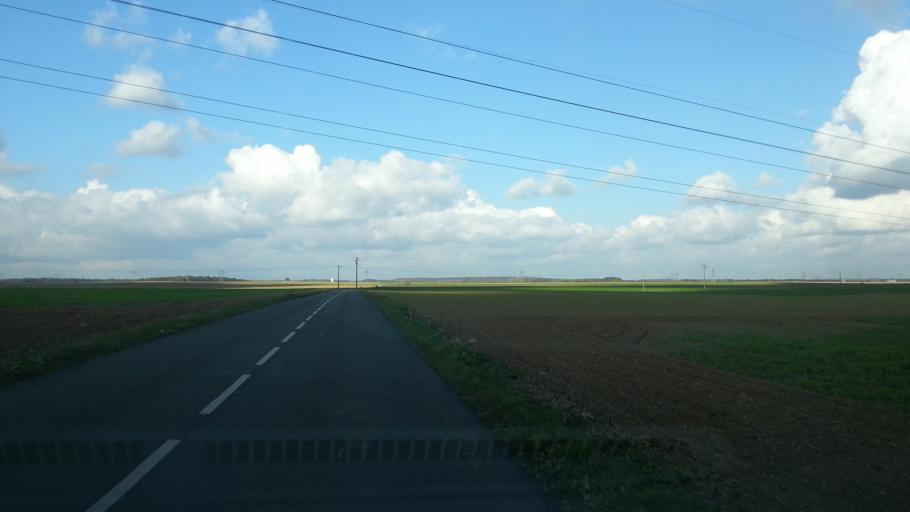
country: FR
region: Picardie
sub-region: Departement de l'Oise
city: Villers-sous-Saint-Leu
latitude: 49.2302
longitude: 2.4128
